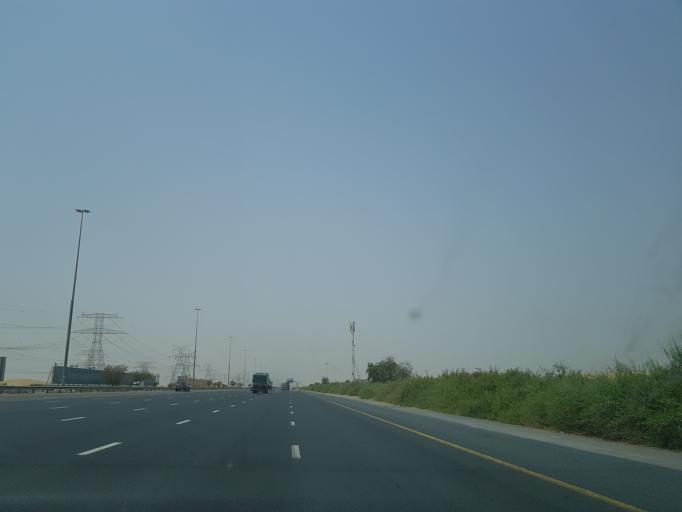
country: AE
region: Ash Shariqah
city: Sharjah
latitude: 25.1211
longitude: 55.4408
